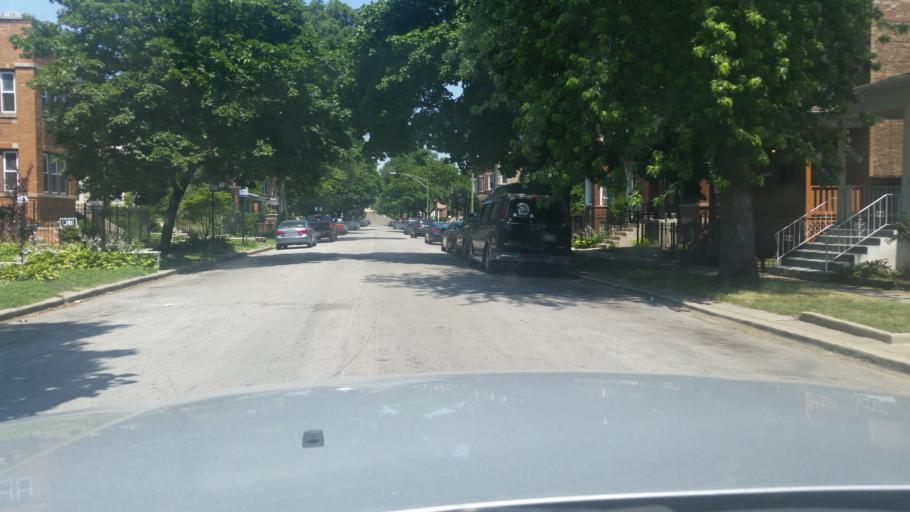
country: US
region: Illinois
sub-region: Cook County
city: Chicago
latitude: 41.7661
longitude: -87.6128
